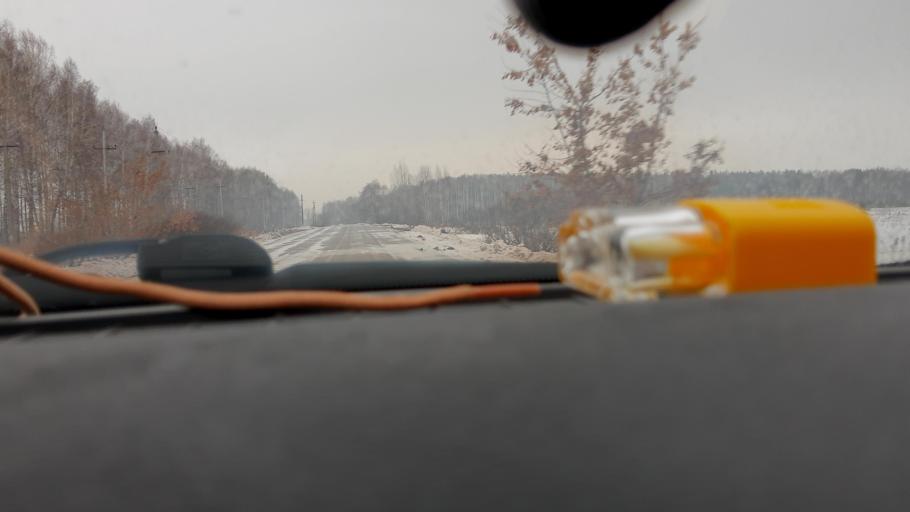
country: RU
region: Bashkortostan
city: Ulukulevo
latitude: 54.4958
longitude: 56.3963
